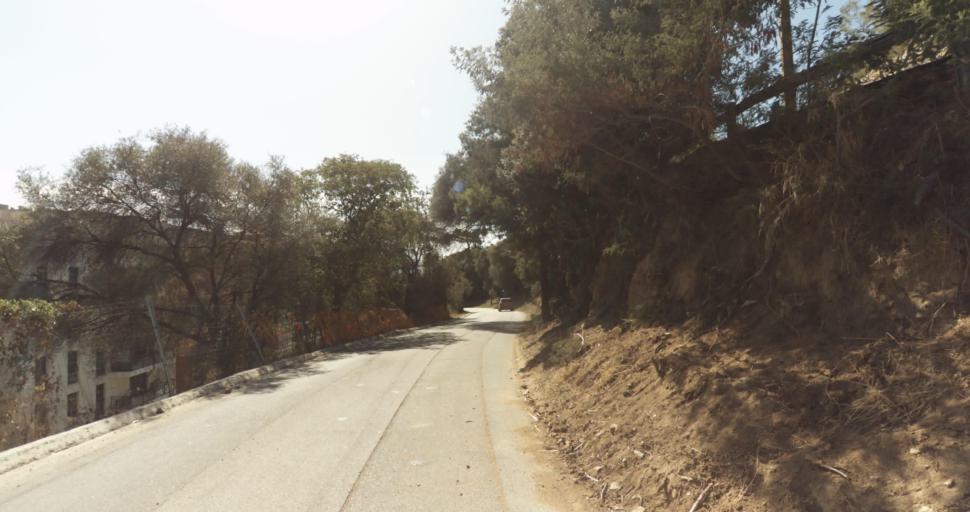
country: FR
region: Corsica
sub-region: Departement de la Corse-du-Sud
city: Ajaccio
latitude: 41.9245
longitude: 8.7289
